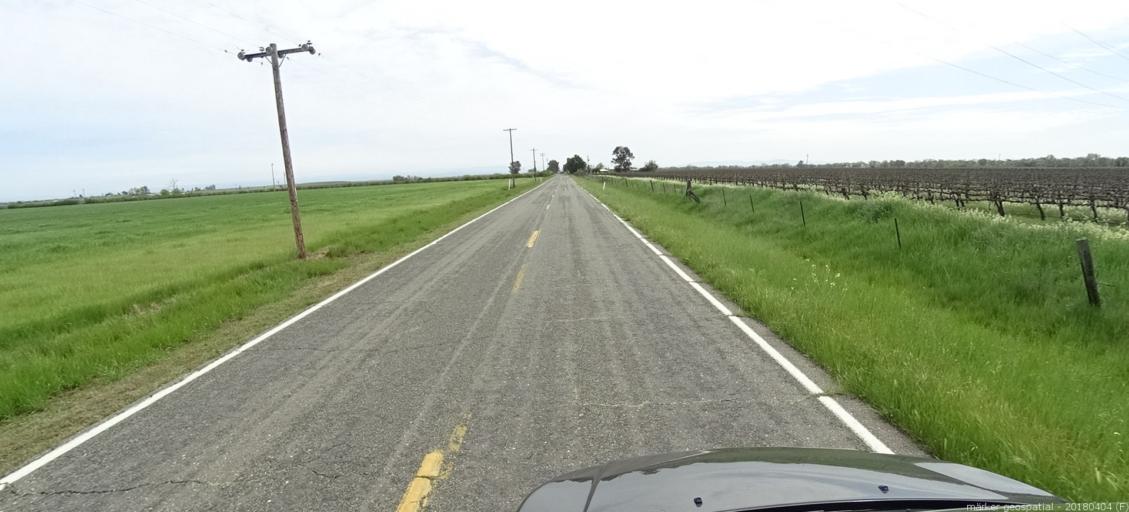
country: US
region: California
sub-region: Sacramento County
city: Herald
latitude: 38.2634
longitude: -121.1935
